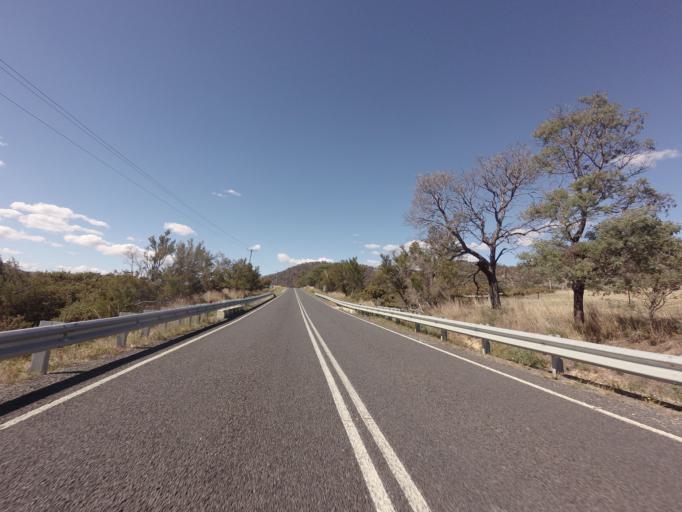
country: AU
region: Tasmania
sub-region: Break O'Day
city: St Helens
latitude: -41.6932
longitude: 147.8677
